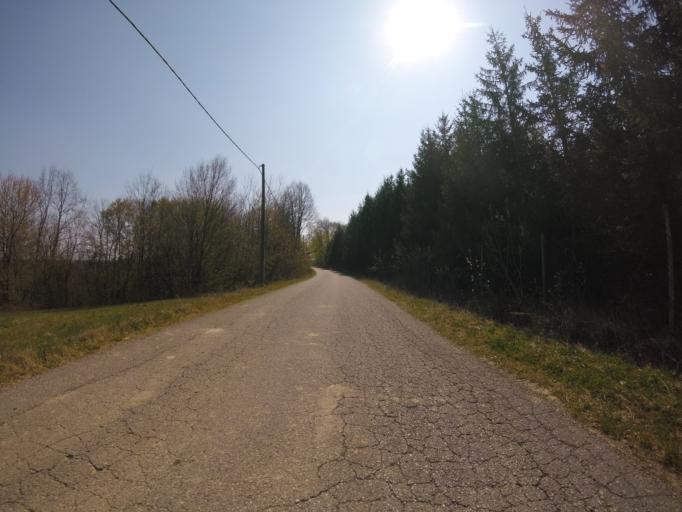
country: HR
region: Grad Zagreb
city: Strmec
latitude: 45.5919
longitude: 15.9239
